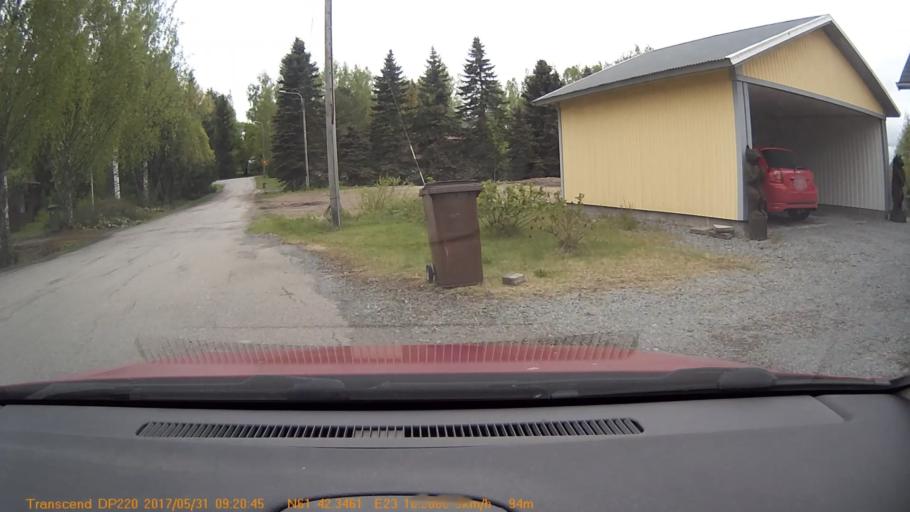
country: FI
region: Pirkanmaa
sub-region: Tampere
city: Viljakkala
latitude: 61.7057
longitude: 23.2715
